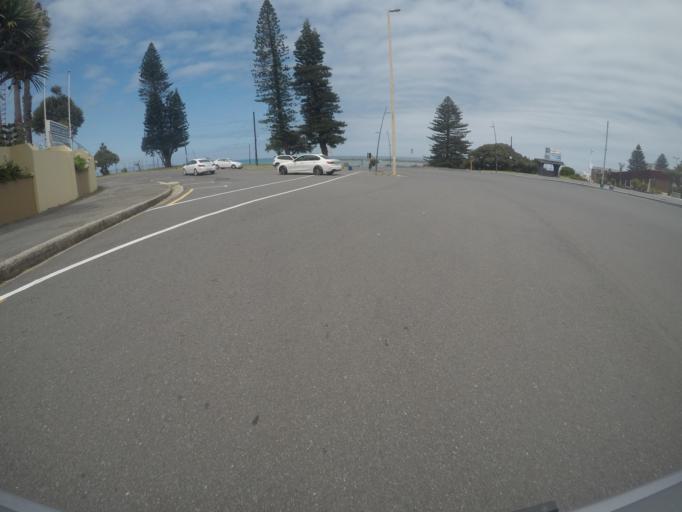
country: ZA
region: Eastern Cape
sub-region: Buffalo City Metropolitan Municipality
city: East London
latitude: -33.0221
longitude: 27.9149
